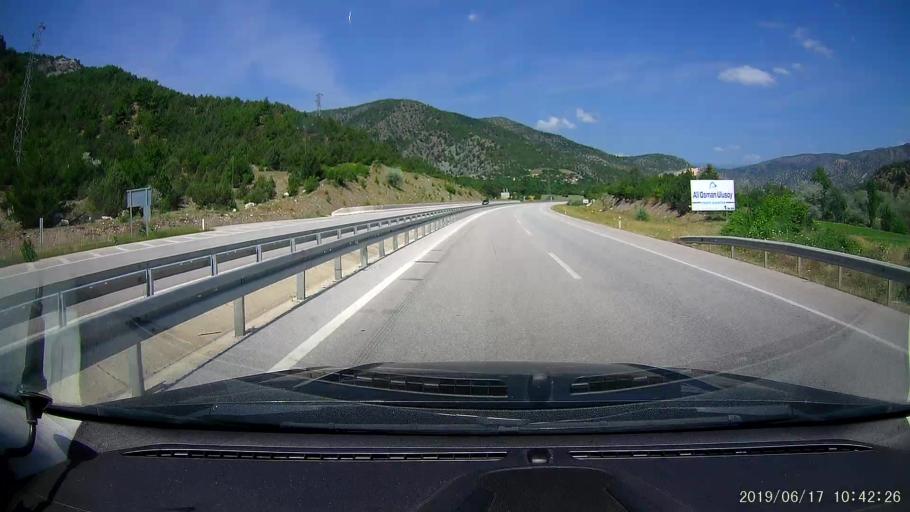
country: TR
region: Corum
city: Hacihamza
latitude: 41.0479
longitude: 34.5537
